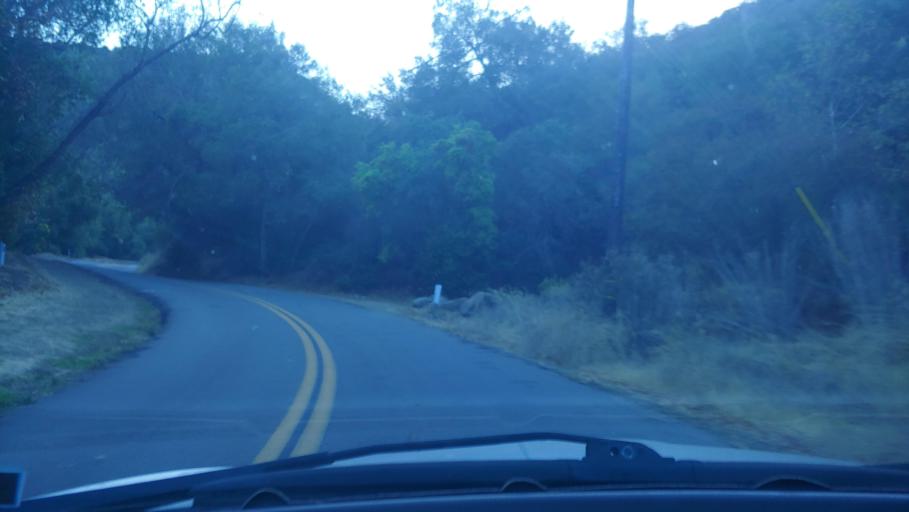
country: US
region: California
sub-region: Santa Barbara County
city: Goleta
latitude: 34.5239
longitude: -119.8381
